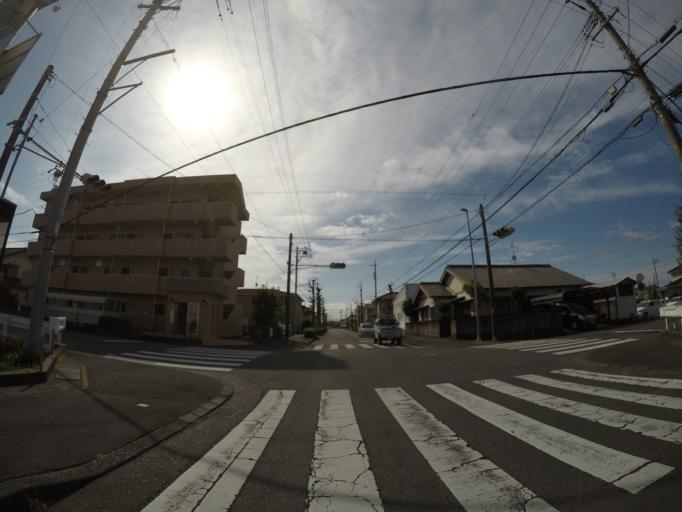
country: JP
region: Shizuoka
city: Yaizu
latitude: 34.8571
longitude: 138.3067
